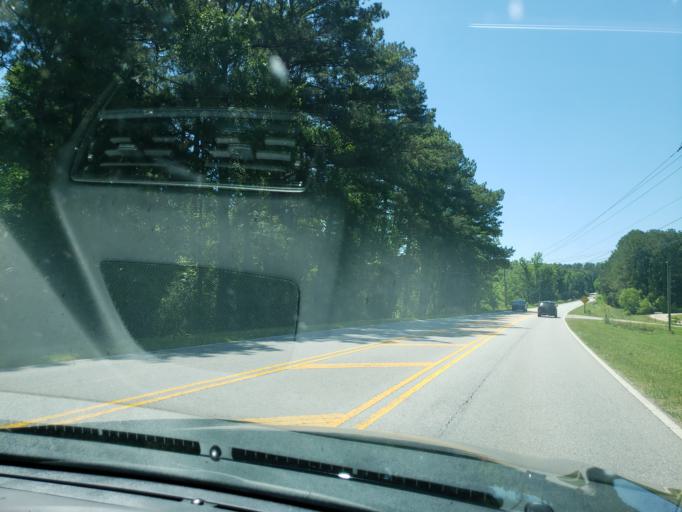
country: US
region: Alabama
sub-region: Lee County
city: Auburn
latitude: 32.6514
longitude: -85.4840
